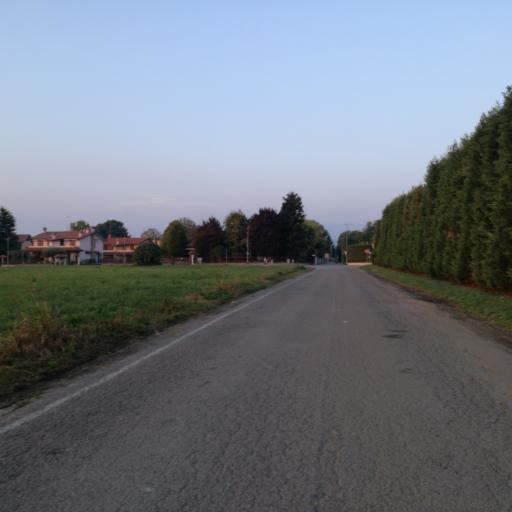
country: IT
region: Lombardy
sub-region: Provincia di Lecco
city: Verderio Inferiore
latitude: 45.6588
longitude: 9.4358
